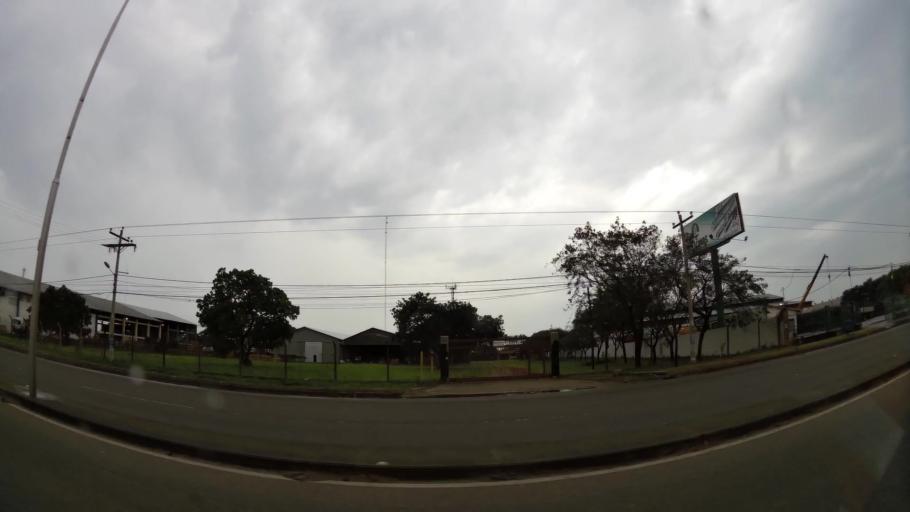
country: BO
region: Santa Cruz
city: Santa Cruz de la Sierra
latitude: -17.7749
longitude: -63.1340
